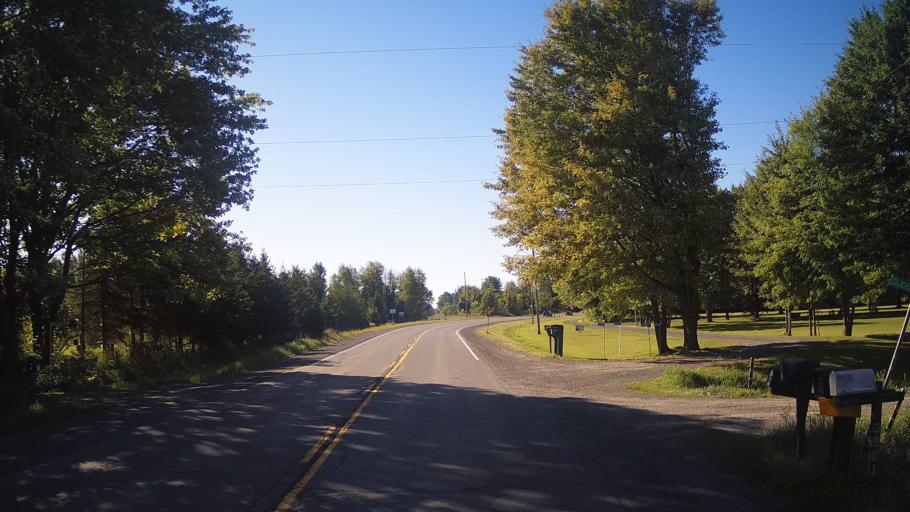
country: CA
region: Ontario
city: Bells Corners
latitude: 45.1074
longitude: -75.6143
